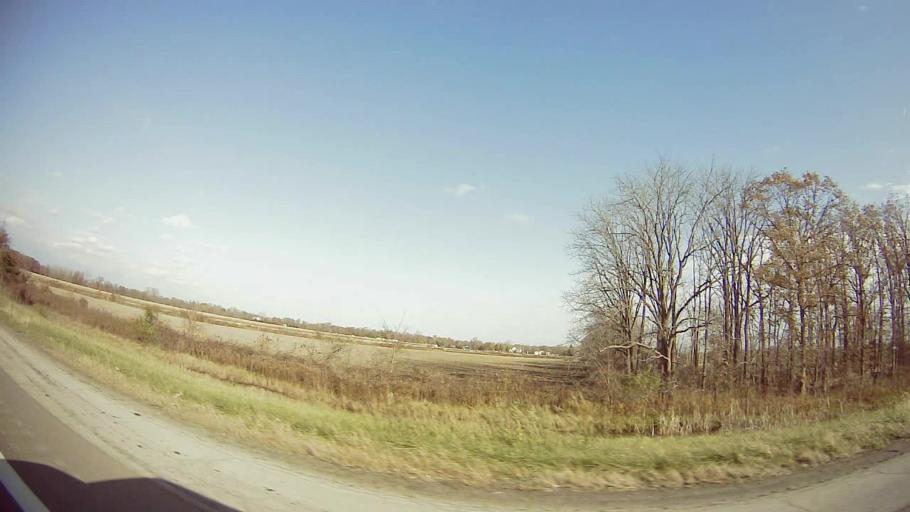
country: US
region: Michigan
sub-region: Monroe County
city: Carleton
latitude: 42.0525
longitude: -83.3542
